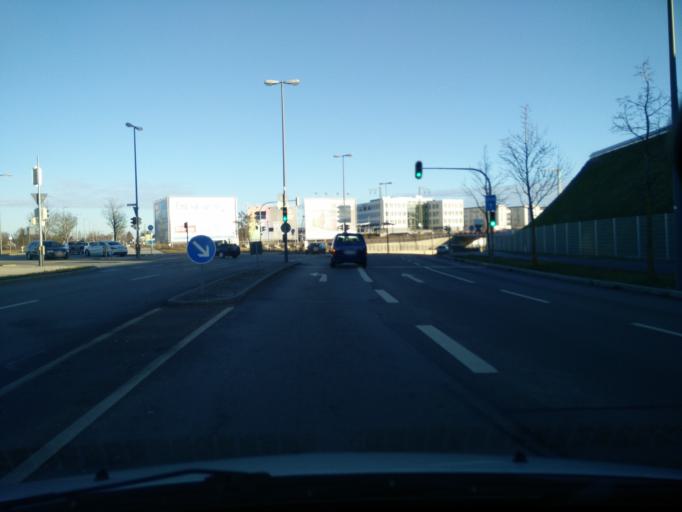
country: DE
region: Bavaria
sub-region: Upper Bavaria
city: Germering
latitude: 48.1403
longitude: 11.4063
